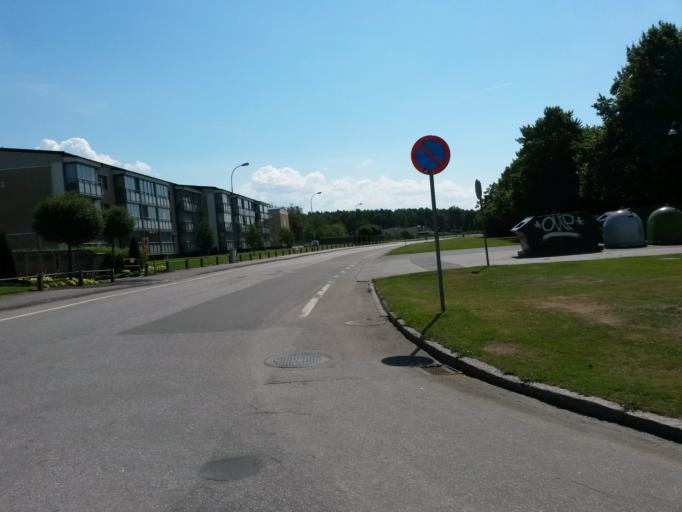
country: SE
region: Vaestra Goetaland
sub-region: Lidkopings Kommun
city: Lidkoping
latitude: 58.4921
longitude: 13.1558
